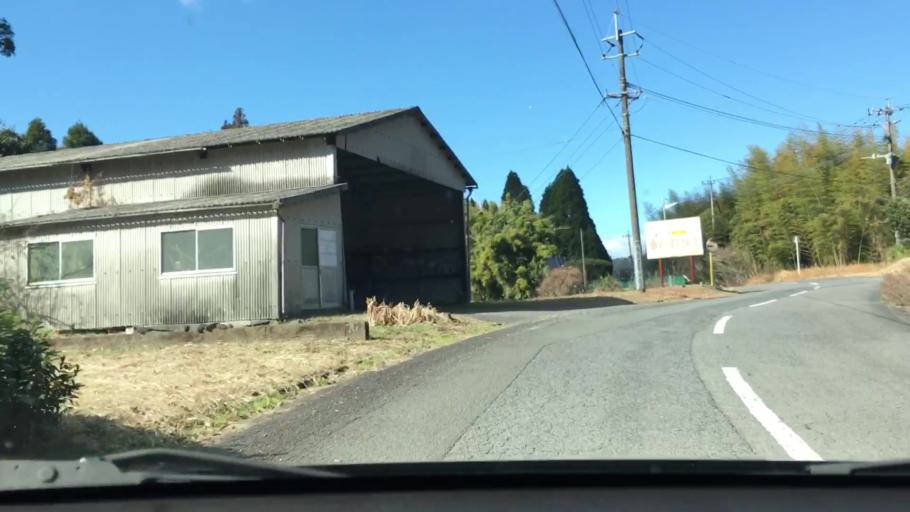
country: JP
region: Kagoshima
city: Ijuin
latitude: 31.7311
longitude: 130.4190
